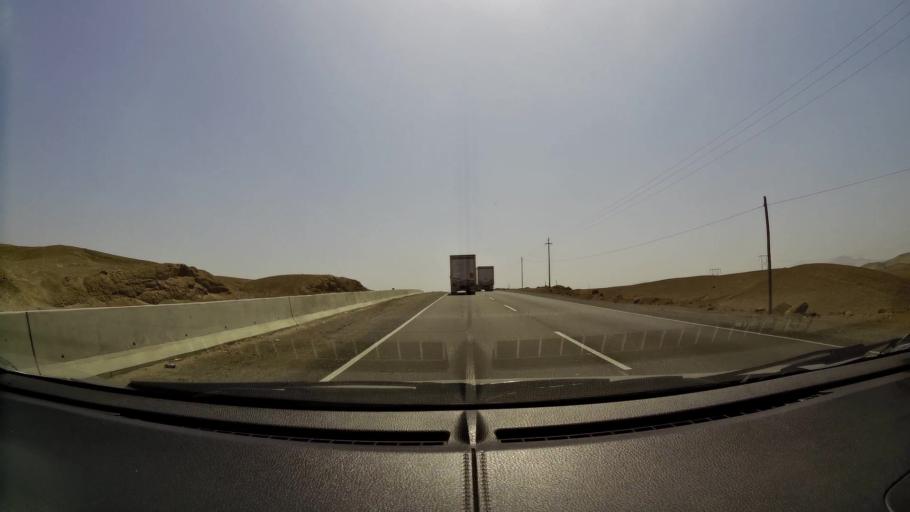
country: PE
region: Ancash
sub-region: Provincia de Huarmey
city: Huarmey
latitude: -10.1856
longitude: -78.0663
